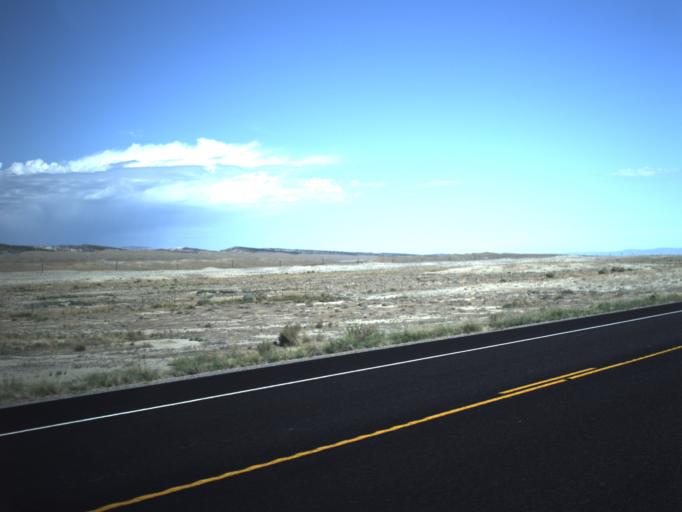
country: US
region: Utah
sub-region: Carbon County
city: East Carbon City
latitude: 39.1718
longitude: -110.3382
